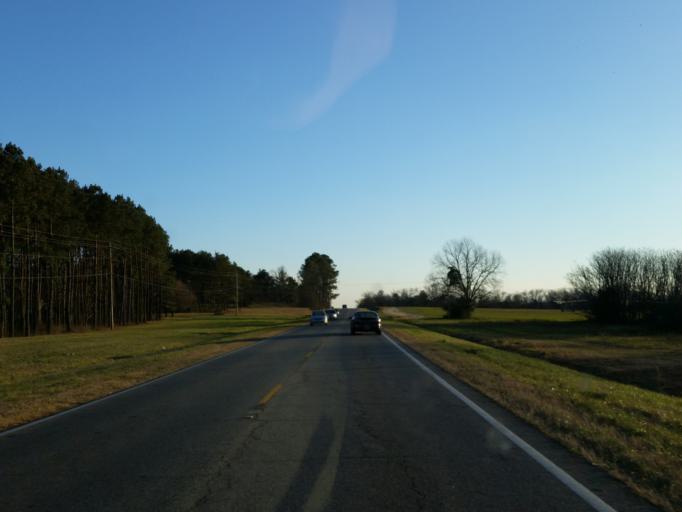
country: US
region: Georgia
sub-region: Crisp County
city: Cordele
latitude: 32.0147
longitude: -83.7920
